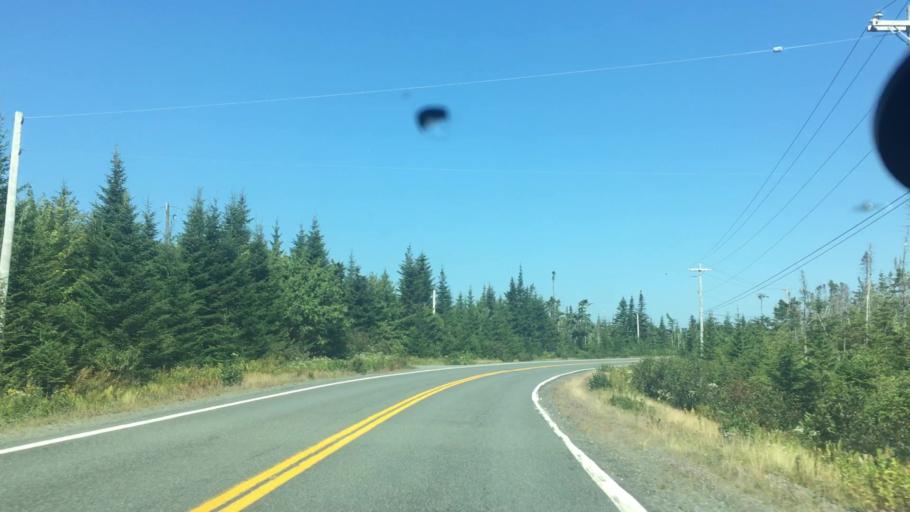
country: CA
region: Nova Scotia
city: Antigonish
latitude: 44.9861
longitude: -62.0969
